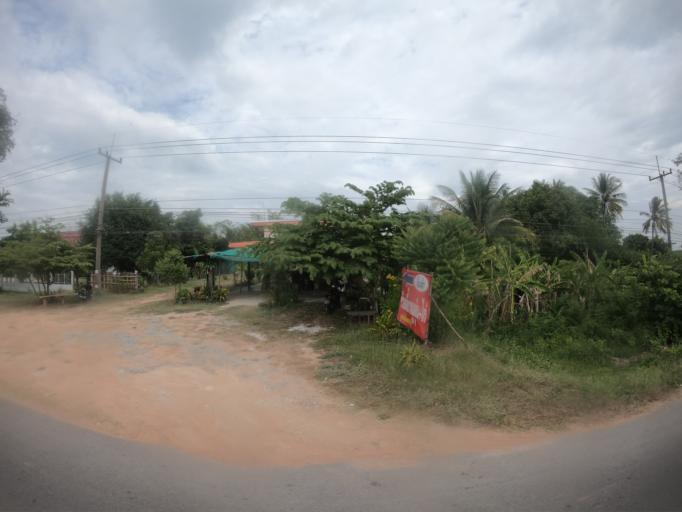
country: TH
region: Maha Sarakham
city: Maha Sarakham
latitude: 16.1531
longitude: 103.3757
